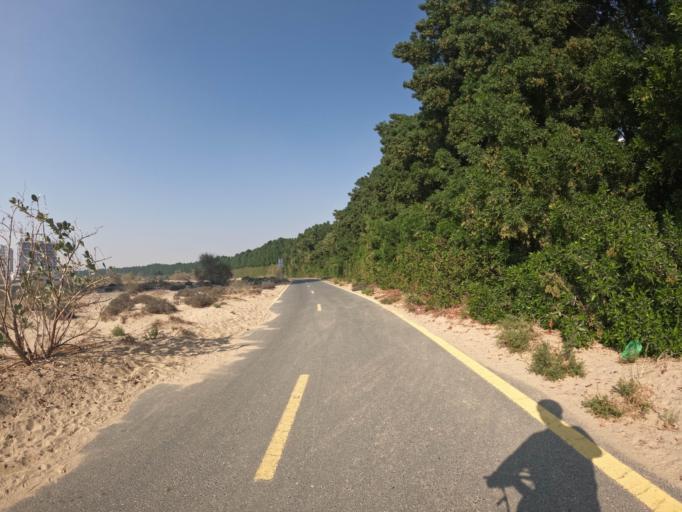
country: AE
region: Dubai
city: Dubai
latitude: 25.0979
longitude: 55.3176
